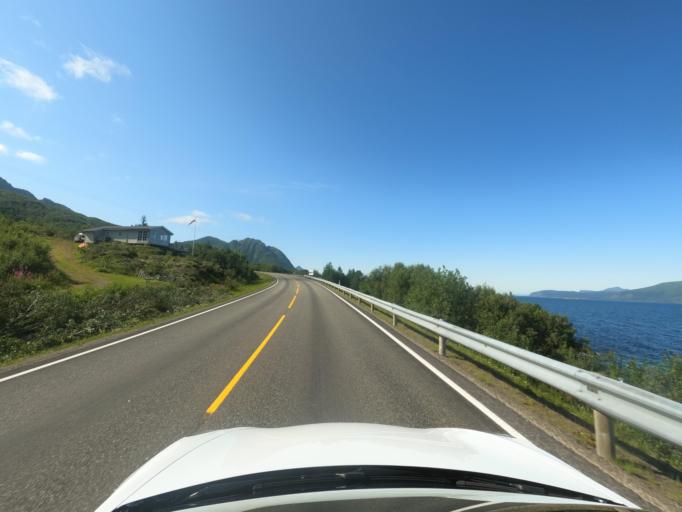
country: NO
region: Nordland
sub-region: Hadsel
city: Stokmarknes
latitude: 68.4626
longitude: 15.0978
